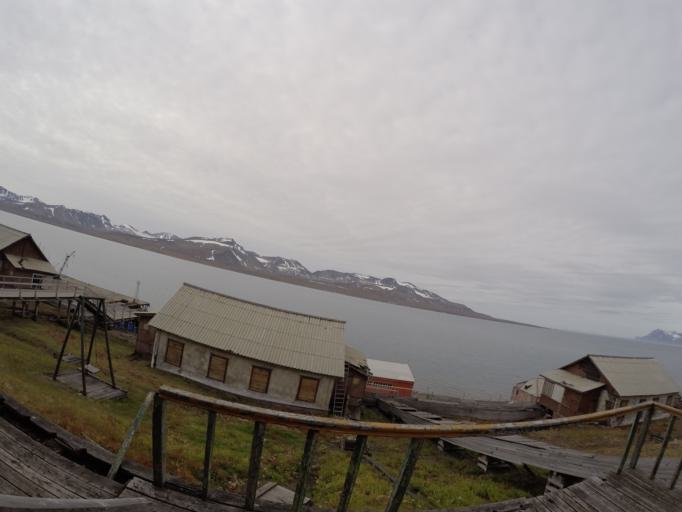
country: SJ
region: Svalbard
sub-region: Spitsbergen
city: Longyearbyen
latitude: 78.0655
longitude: 14.2061
